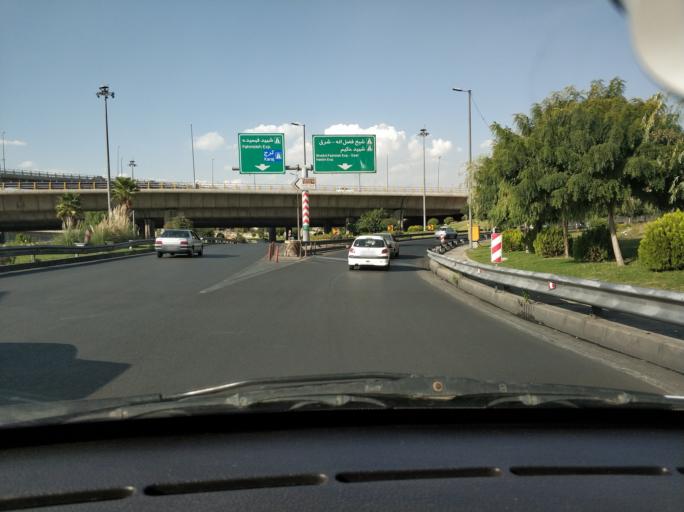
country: IR
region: Tehran
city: Tehran
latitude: 35.7108
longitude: 51.3369
